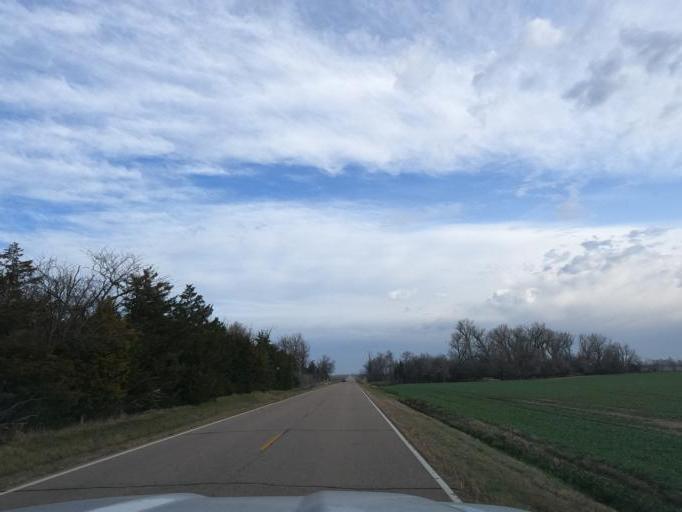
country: US
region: Kansas
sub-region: Reno County
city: Nickerson
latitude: 38.0193
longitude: -98.1788
